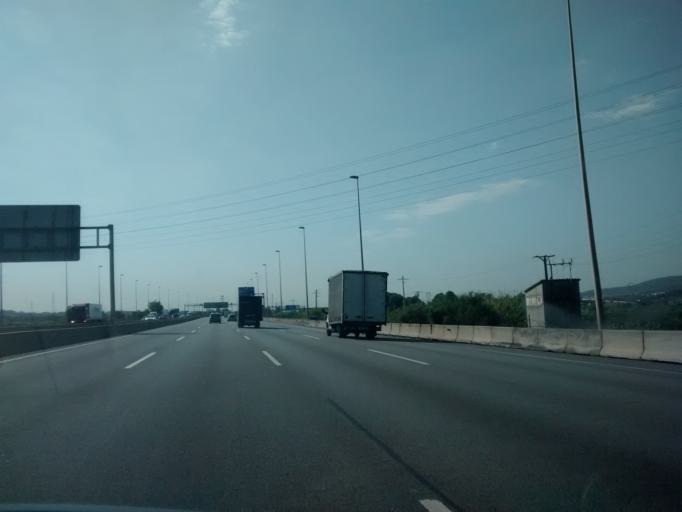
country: ES
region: Catalonia
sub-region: Provincia de Barcelona
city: Sant Vicenc dels Horts
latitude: 41.4013
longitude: 2.0192
